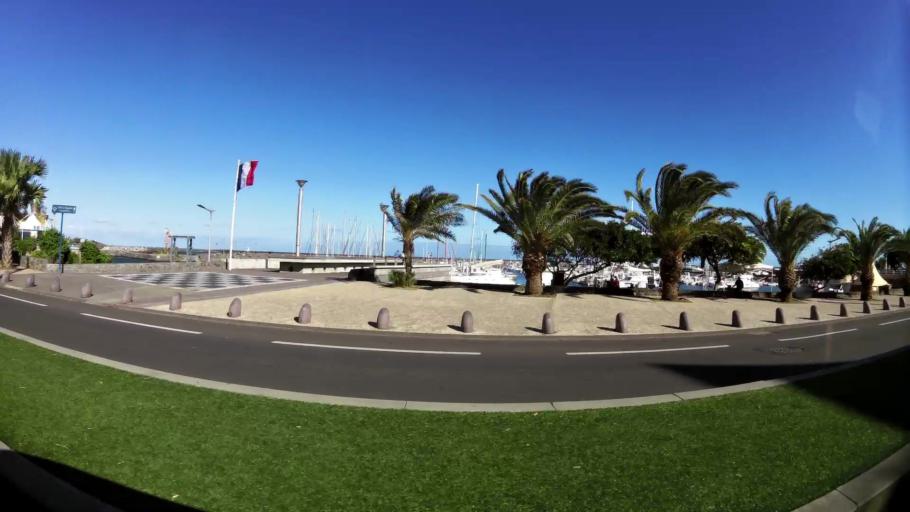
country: RE
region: Reunion
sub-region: Reunion
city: Saint-Pierre
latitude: -21.3436
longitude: 55.4762
